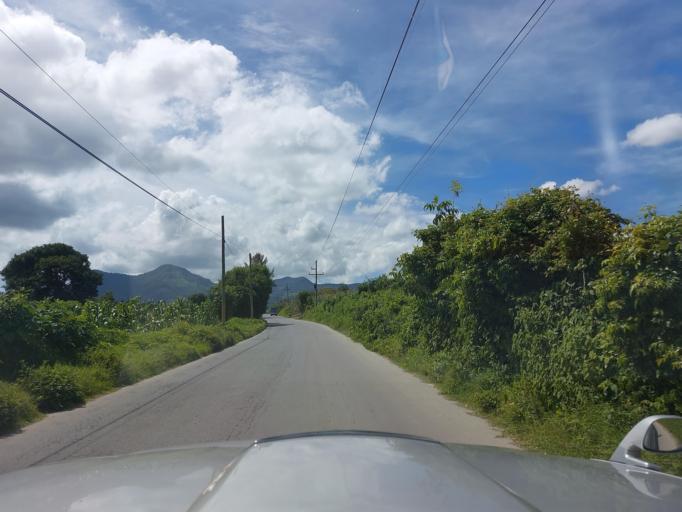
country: GT
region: Chimaltenango
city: Parramos
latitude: 14.6145
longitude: -90.8214
